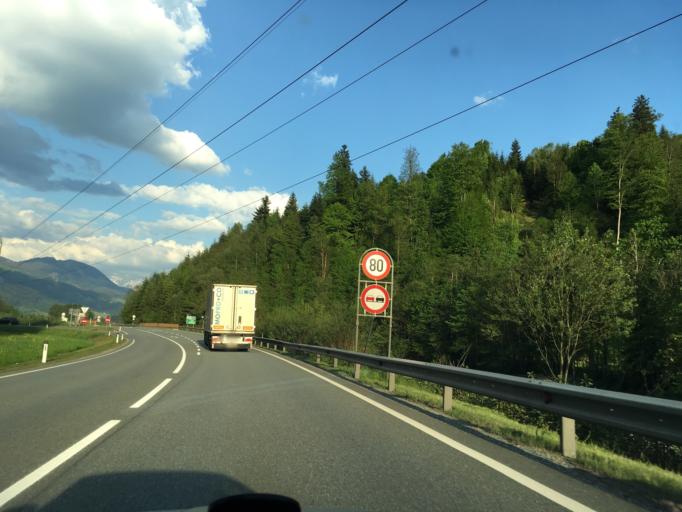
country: AT
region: Tyrol
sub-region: Politischer Bezirk Kitzbuhel
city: Oberndorf in Tirol
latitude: 47.5221
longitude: 12.3886
